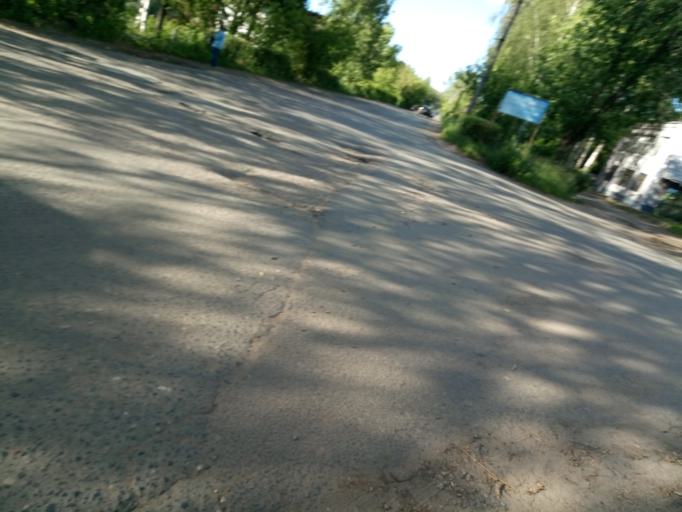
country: RU
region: Jaroslavl
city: Yaroslavl
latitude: 57.6413
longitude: 39.9142
